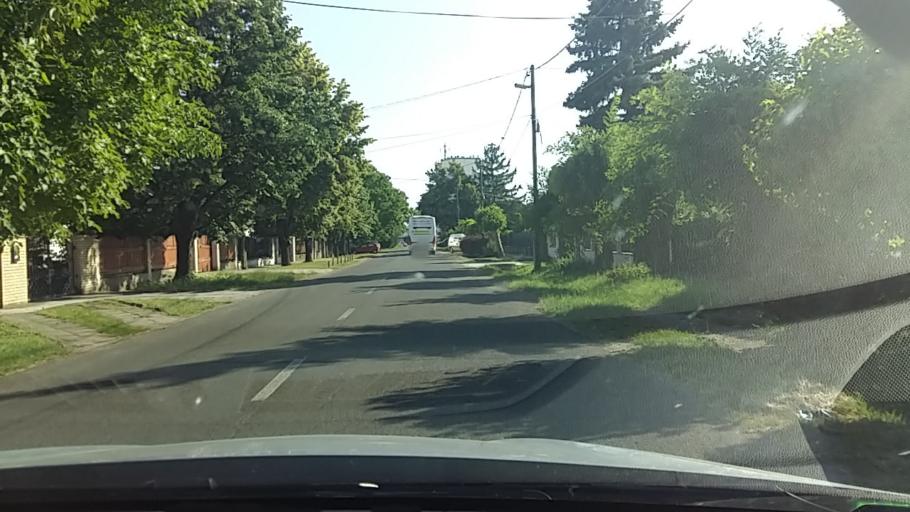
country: HU
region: Heves
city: Gyongyos
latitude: 47.7684
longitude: 19.9215
